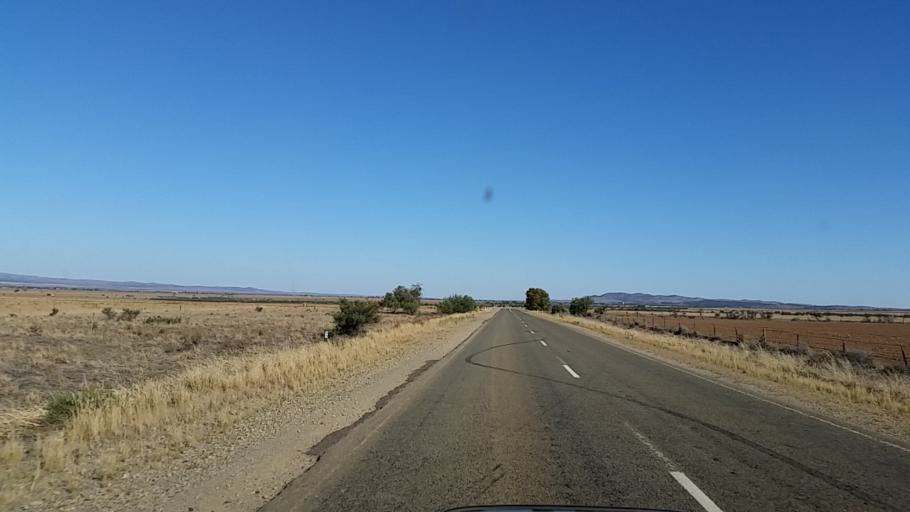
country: AU
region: South Australia
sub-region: Peterborough
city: Peterborough
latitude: -32.6633
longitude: 138.6061
